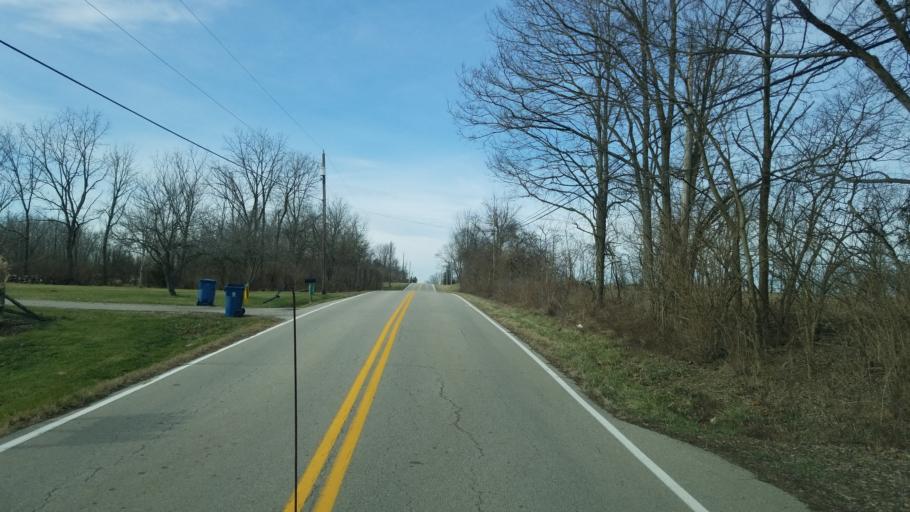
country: US
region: Ohio
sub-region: Warren County
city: Lebanon
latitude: 39.4291
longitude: -84.1441
